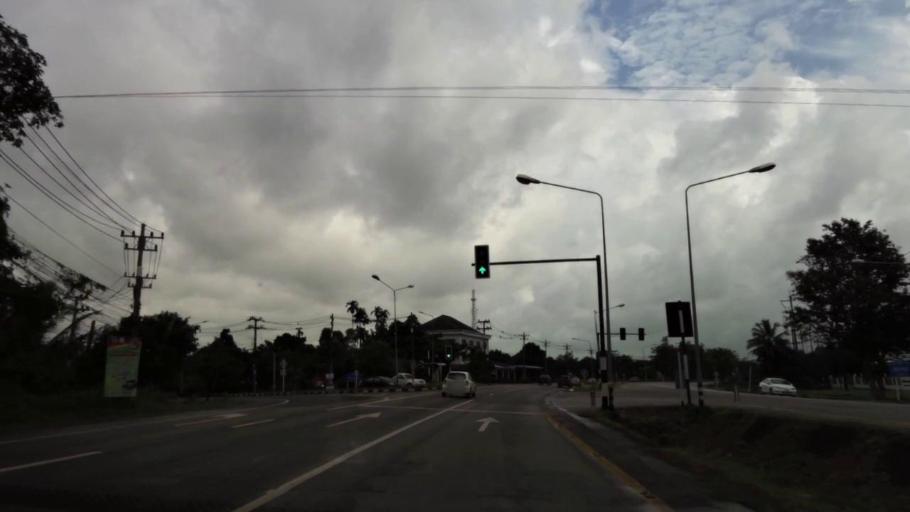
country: TH
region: Chanthaburi
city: Chanthaburi
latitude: 12.5297
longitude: 102.1577
